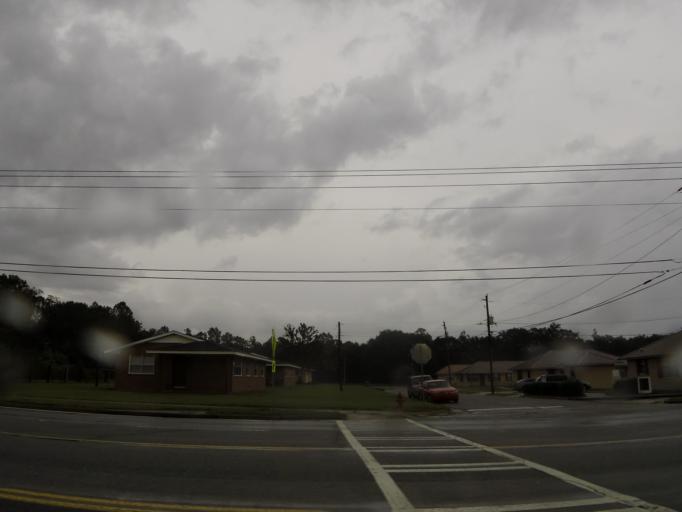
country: US
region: Georgia
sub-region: Wayne County
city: Jesup
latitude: 31.5995
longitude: -81.8713
